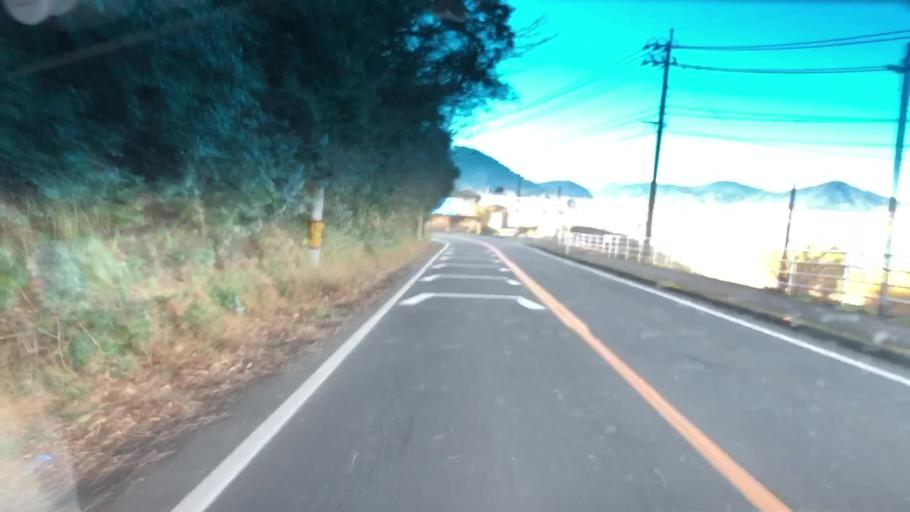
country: JP
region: Kagoshima
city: Satsumasendai
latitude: 31.8168
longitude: 130.2884
